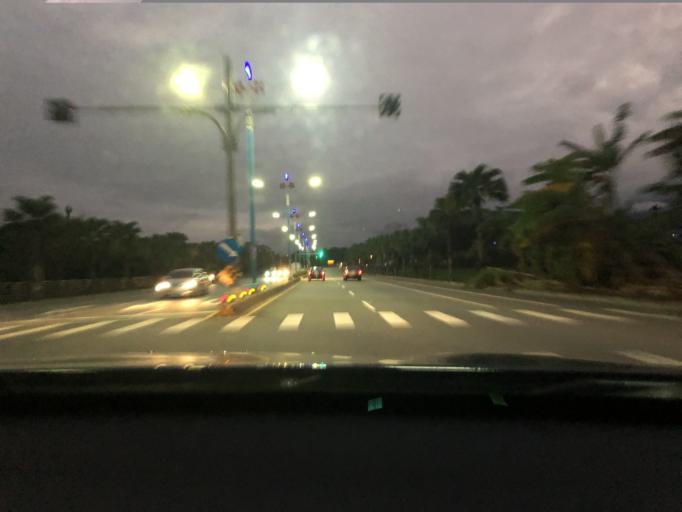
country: TW
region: Taiwan
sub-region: Hualien
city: Hualian
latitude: 23.9545
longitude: 121.5604
